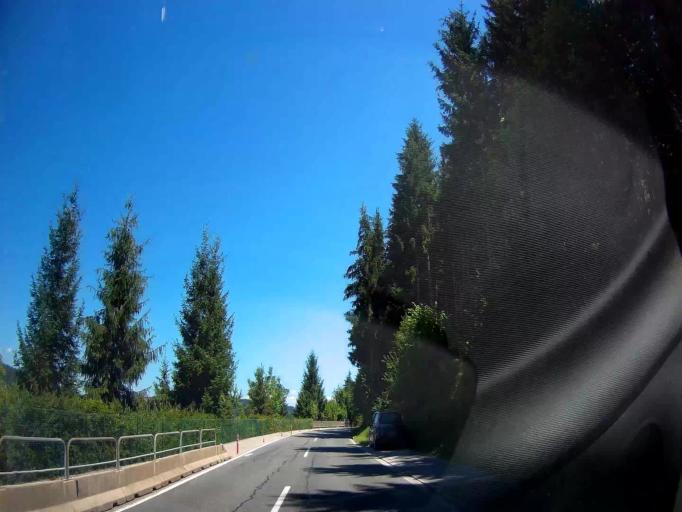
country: AT
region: Carinthia
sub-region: Politischer Bezirk Klagenfurt Land
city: Keutschach am See
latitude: 46.6097
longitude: 14.2230
